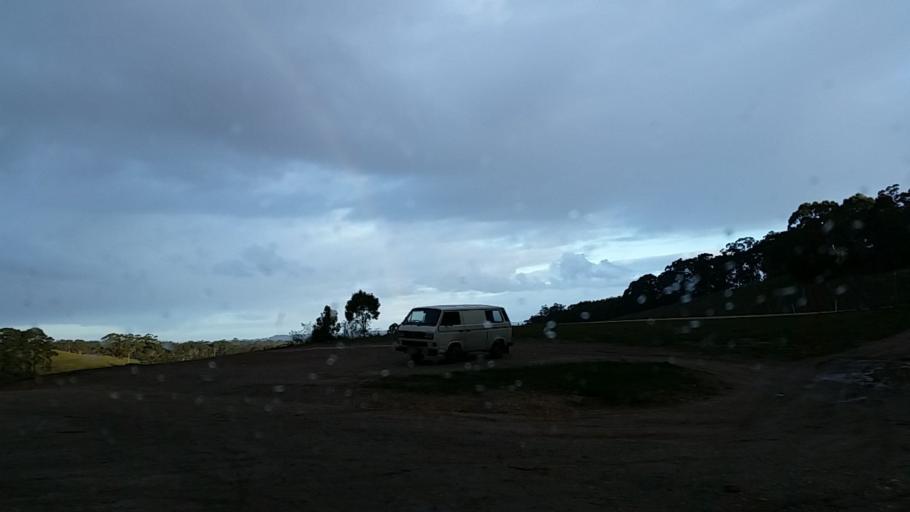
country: AU
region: South Australia
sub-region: Adelaide Hills
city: Lobethal
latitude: -34.8872
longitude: 138.8232
